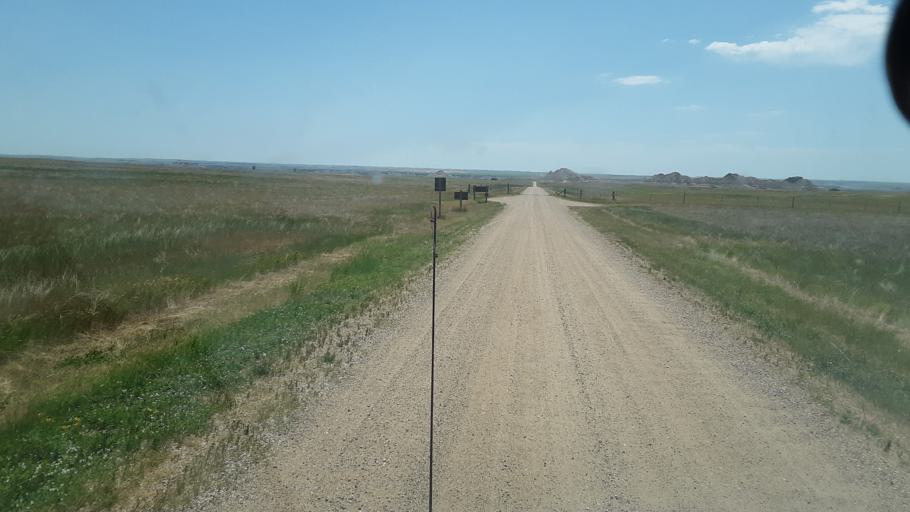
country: US
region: South Dakota
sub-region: Haakon County
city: Philip
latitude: 43.7496
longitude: -101.9996
